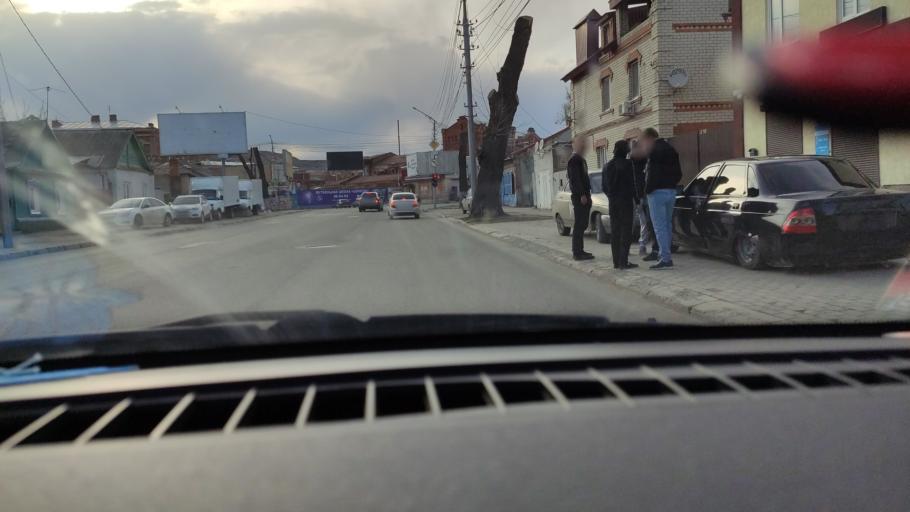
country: RU
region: Saratov
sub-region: Saratovskiy Rayon
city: Saratov
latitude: 51.5501
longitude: 46.0112
